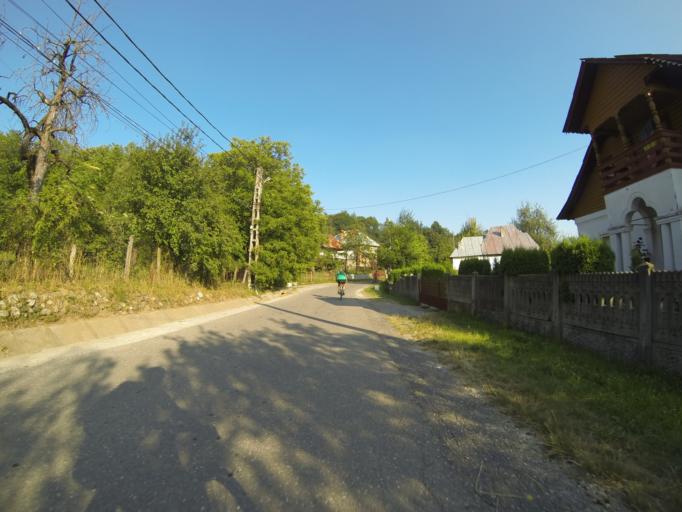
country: RO
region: Valcea
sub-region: Comuna Horezu
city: Horezu
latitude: 45.1698
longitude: 23.9865
